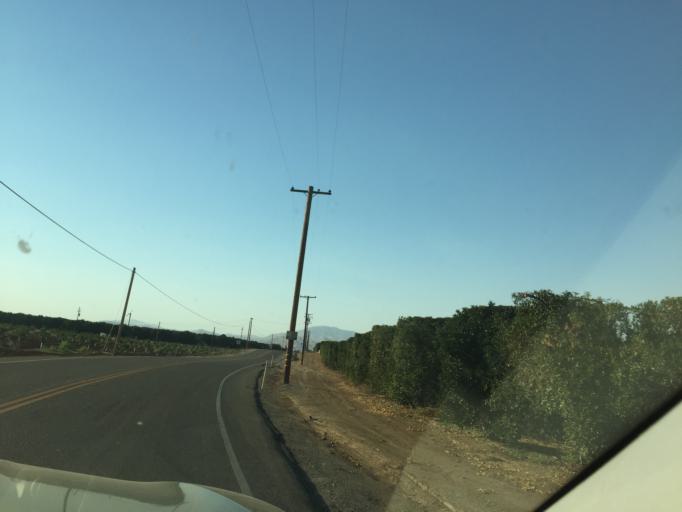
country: US
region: California
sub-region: Fresno County
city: Orange Cove
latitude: 36.6025
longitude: -119.2870
